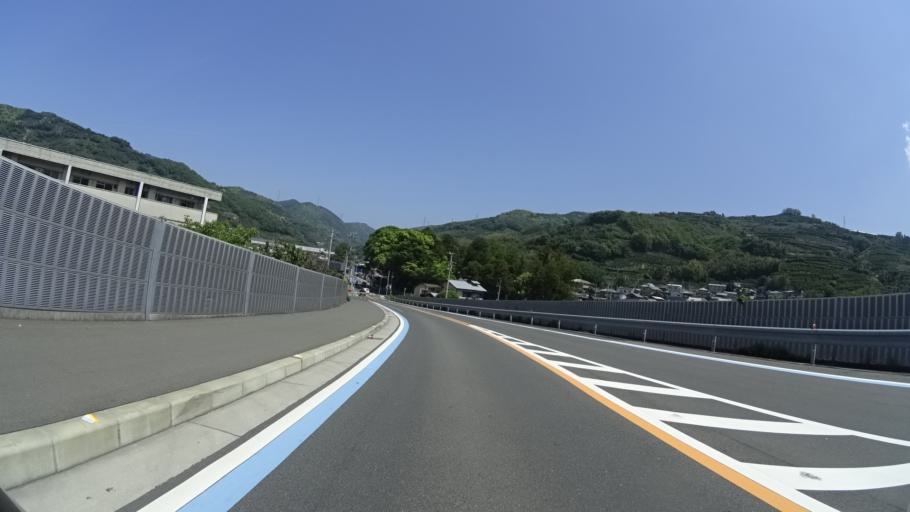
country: JP
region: Ehime
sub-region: Nishiuwa-gun
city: Ikata-cho
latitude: 33.4893
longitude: 132.3975
